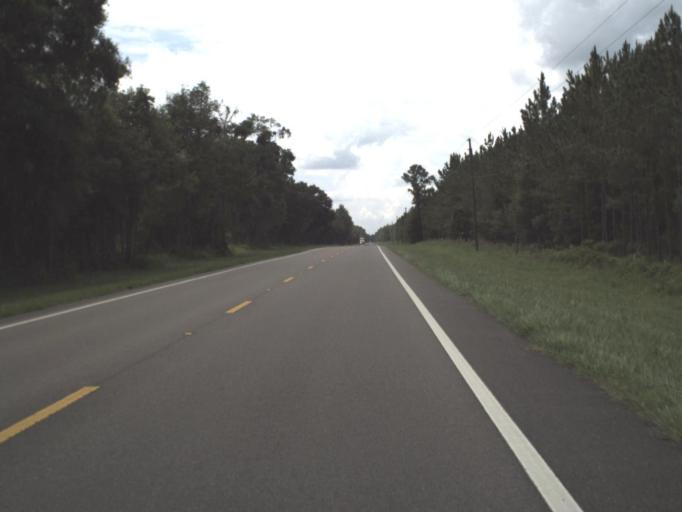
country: US
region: Florida
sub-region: Alachua County
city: Archer
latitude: 29.4664
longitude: -82.4801
